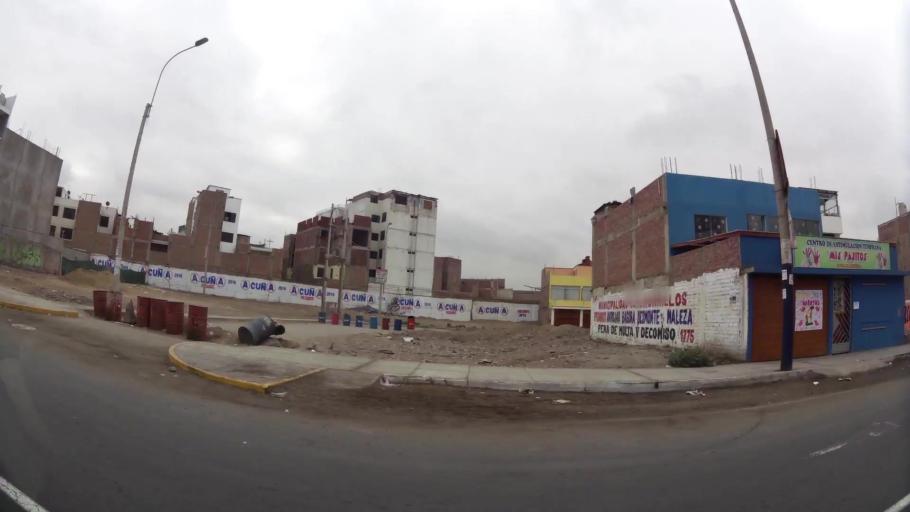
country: PE
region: Lima
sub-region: Lima
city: Surco
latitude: -12.1728
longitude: -76.9919
